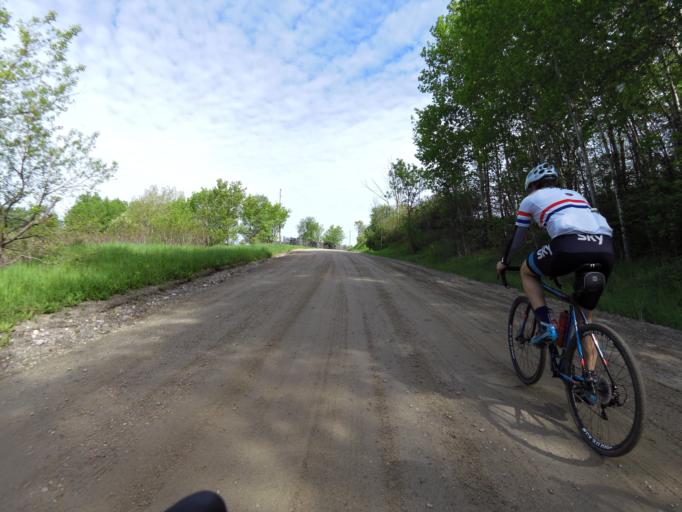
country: CA
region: Quebec
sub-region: Outaouais
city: Wakefield
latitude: 45.6978
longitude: -75.8948
